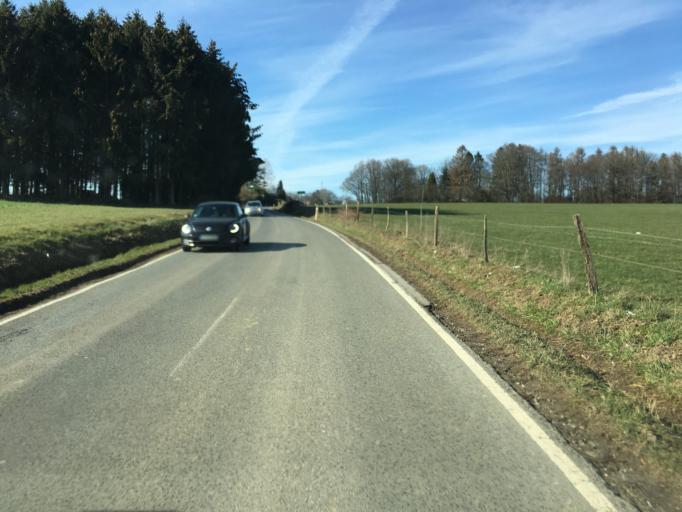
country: DE
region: North Rhine-Westphalia
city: Huckeswagen
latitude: 51.1375
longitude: 7.3146
